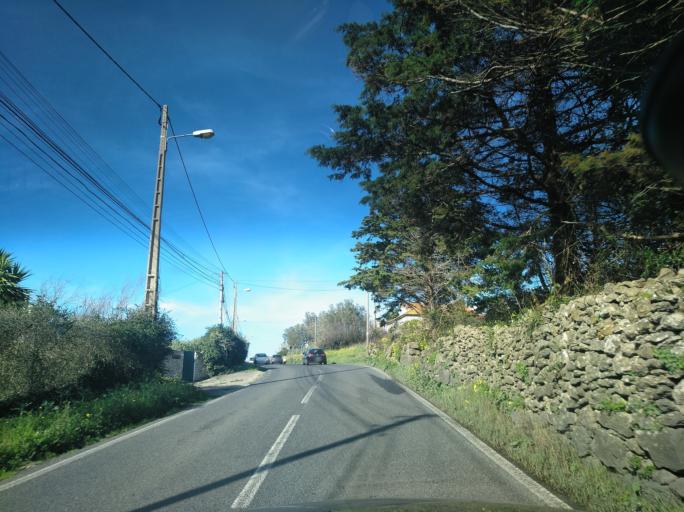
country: PT
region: Lisbon
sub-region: Sintra
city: Pero Pinheiro
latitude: 38.8929
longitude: -9.3268
